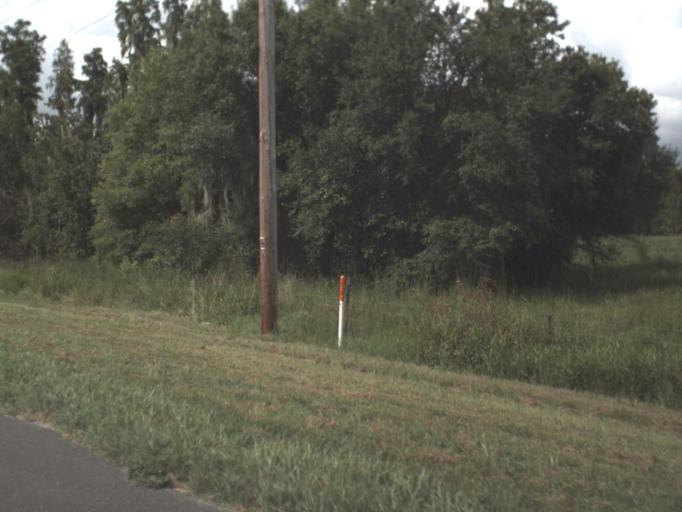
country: US
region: Florida
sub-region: Pasco County
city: Crystal Springs
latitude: 28.1639
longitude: -82.1546
